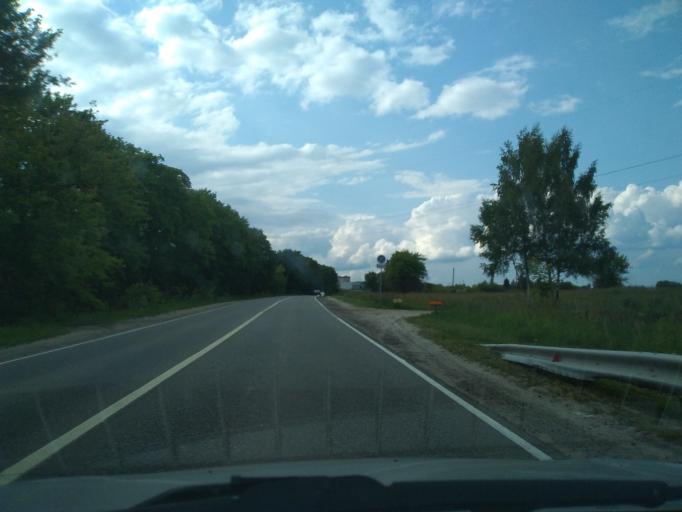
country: RU
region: Moskovskaya
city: Voskresensk
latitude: 55.2994
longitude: 38.6639
